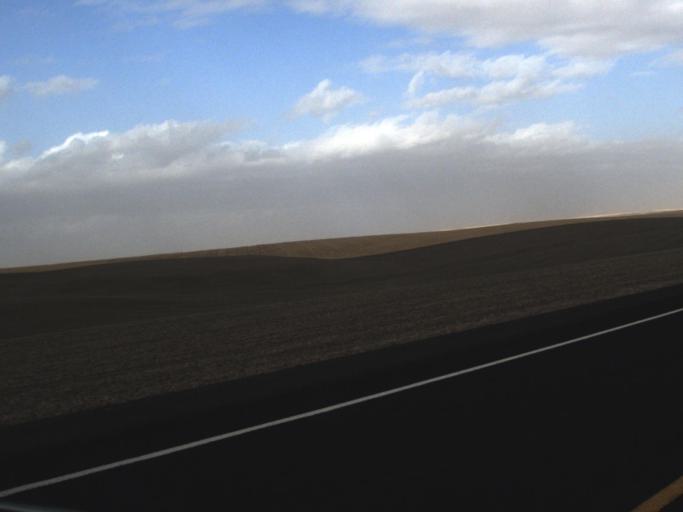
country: US
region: Washington
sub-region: Lincoln County
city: Davenport
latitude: 47.4671
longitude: -118.2979
